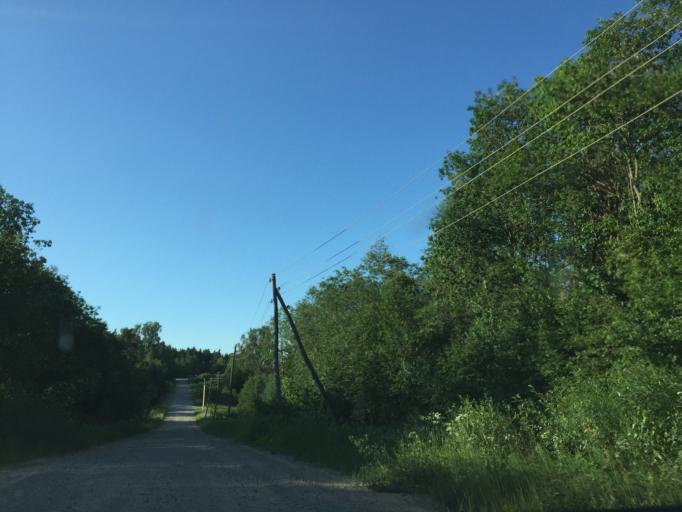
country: LV
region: Kandava
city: Kandava
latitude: 56.8543
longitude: 22.6930
